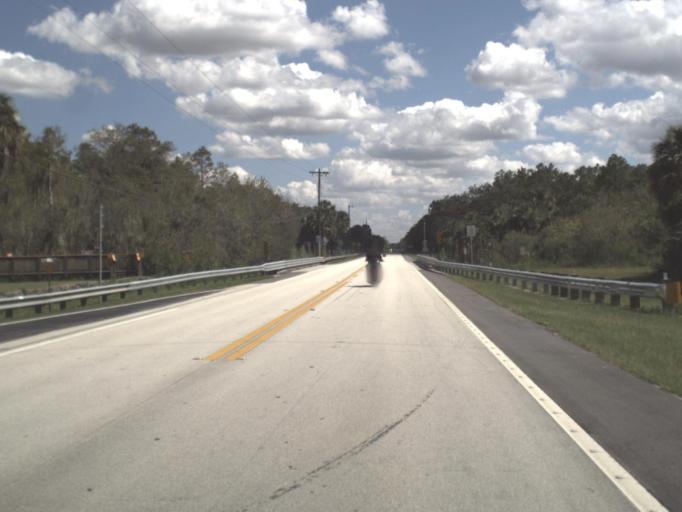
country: US
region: Florida
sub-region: Collier County
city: Marco
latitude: 25.8878
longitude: -81.2627
